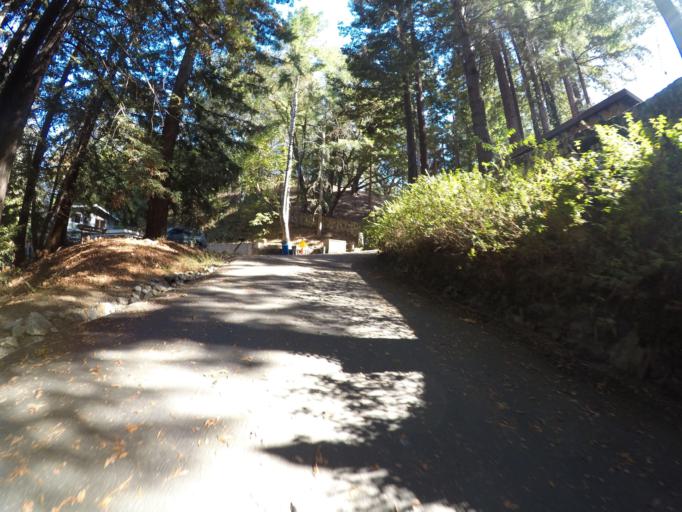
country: US
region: California
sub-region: Santa Cruz County
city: Scotts Valley
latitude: 37.0539
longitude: -122.0205
